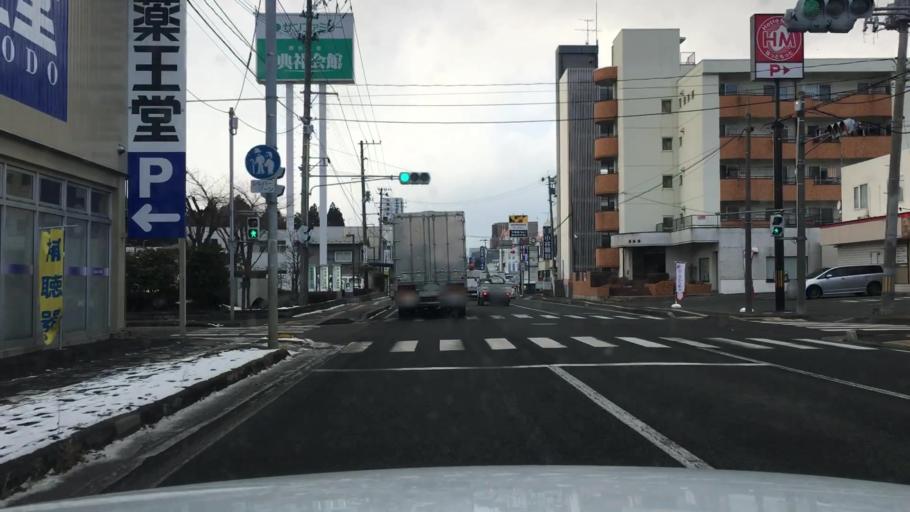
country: JP
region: Iwate
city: Morioka-shi
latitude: 39.6938
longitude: 141.1695
